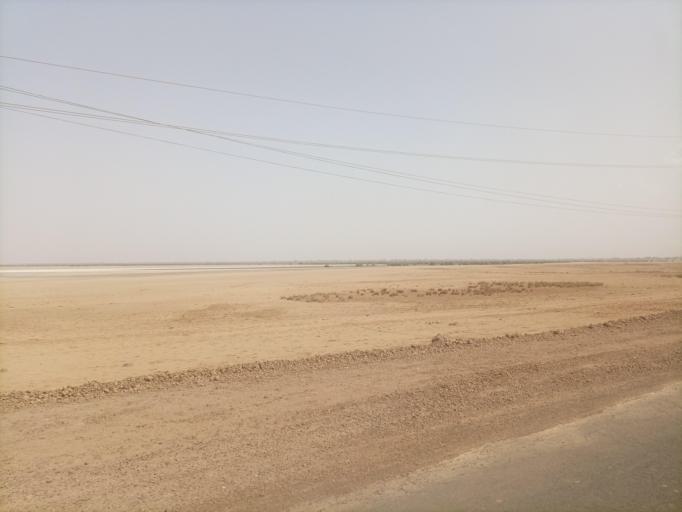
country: SN
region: Fatick
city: Foundiougne
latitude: 14.1537
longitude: -16.4702
